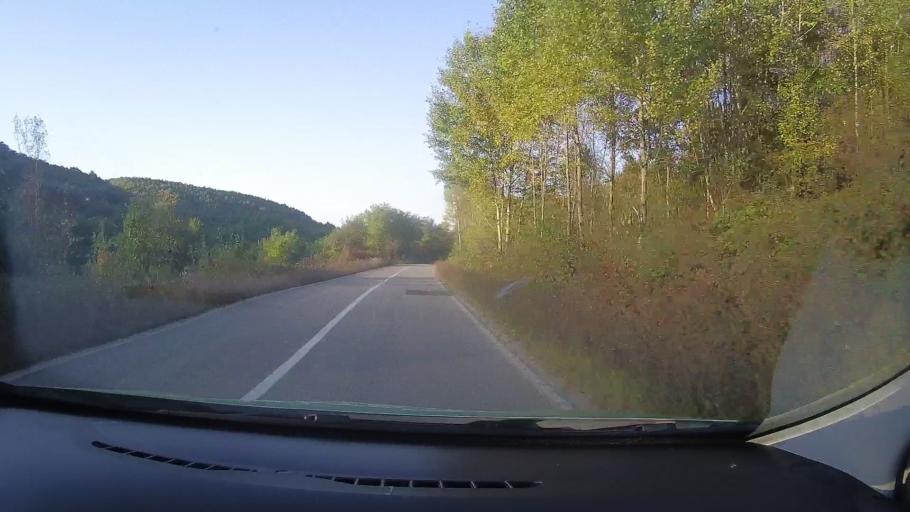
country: RO
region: Timis
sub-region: Comuna Fardea
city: Fardea
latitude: 45.6980
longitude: 22.1603
